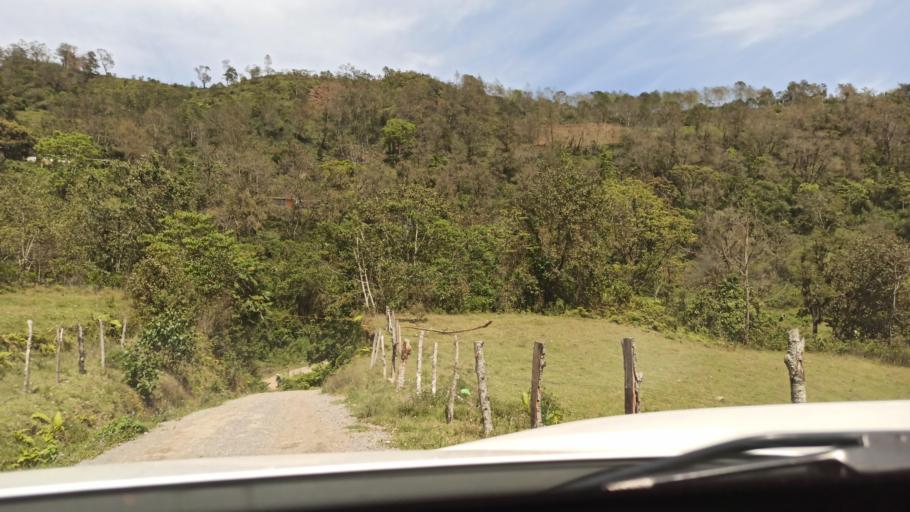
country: MX
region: Veracruz
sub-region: La Perla
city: Metlac Hernandez (Metlac Primero)
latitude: 18.9766
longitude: -97.1072
